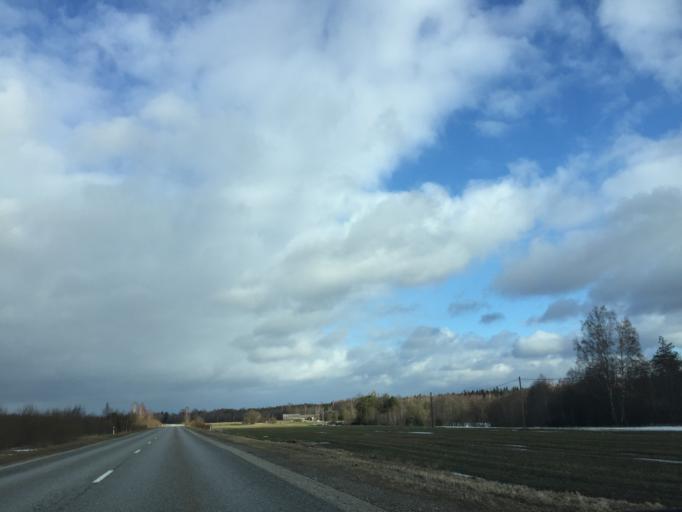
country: LV
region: Aloja
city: Staicele
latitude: 57.8789
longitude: 24.5906
